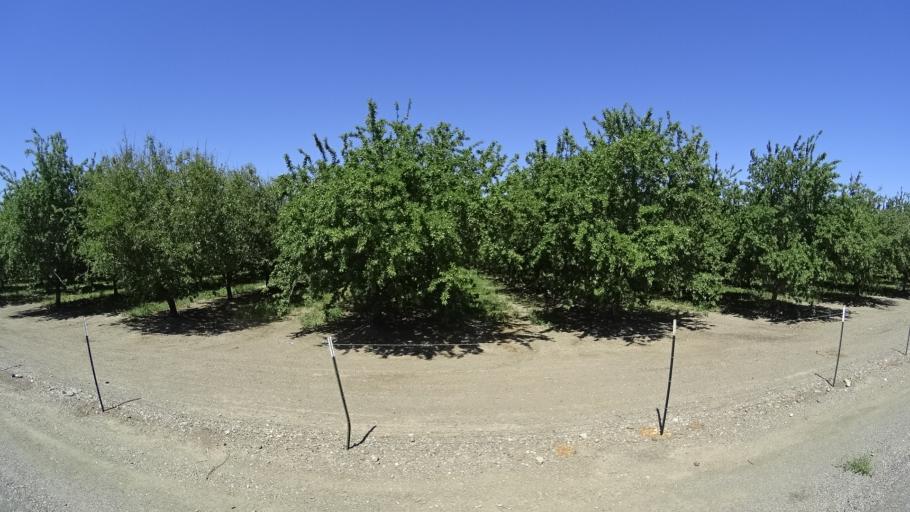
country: US
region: California
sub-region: Glenn County
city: Orland
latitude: 39.7417
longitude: -122.1656
